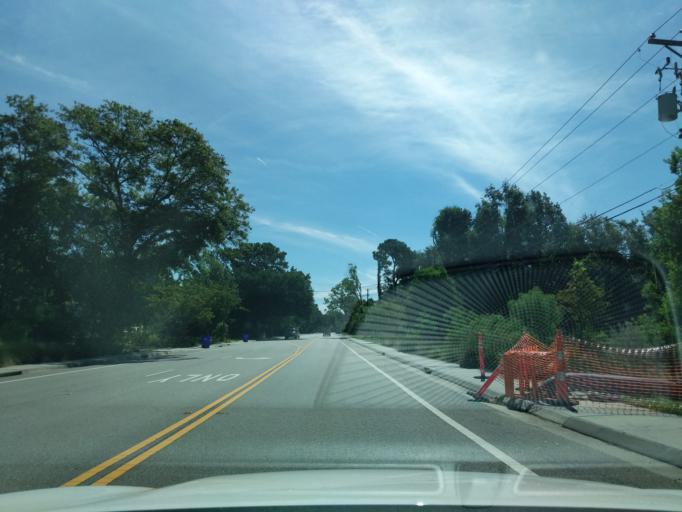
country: US
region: South Carolina
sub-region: Charleston County
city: Charleston
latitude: 32.7421
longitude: -79.9293
